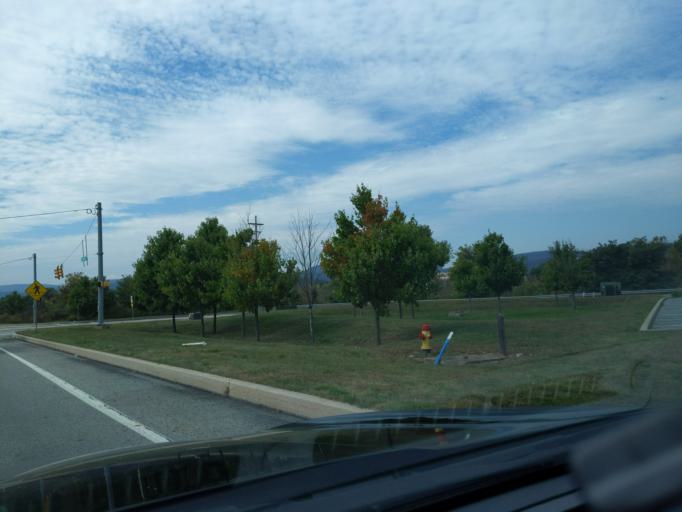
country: US
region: Pennsylvania
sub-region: Blair County
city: Lakemont
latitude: 40.4864
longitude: -78.3880
